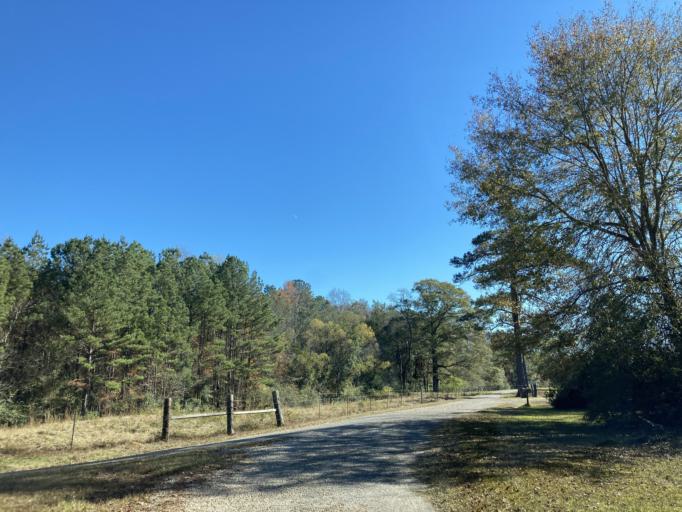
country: US
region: Mississippi
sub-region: Lamar County
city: Sumrall
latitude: 31.3101
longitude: -89.6512
